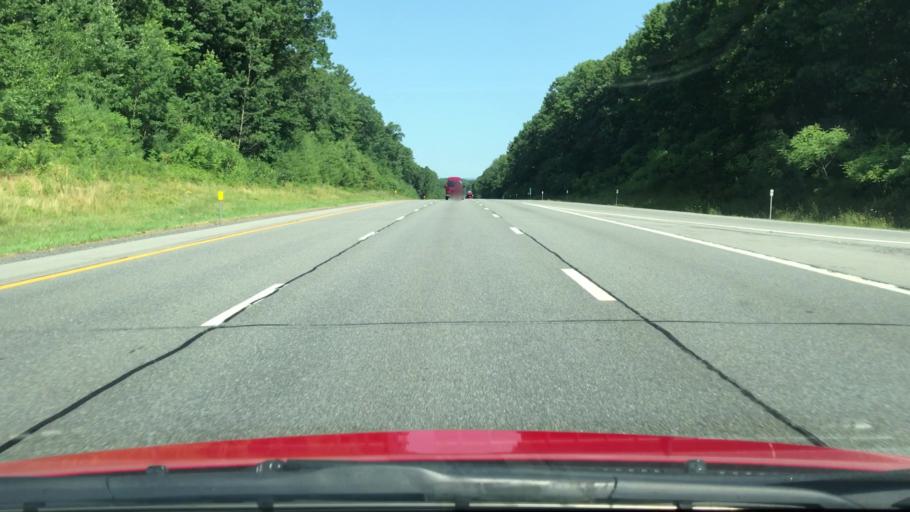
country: US
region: New York
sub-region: Saratoga County
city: Country Knolls
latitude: 42.9040
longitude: -73.7869
